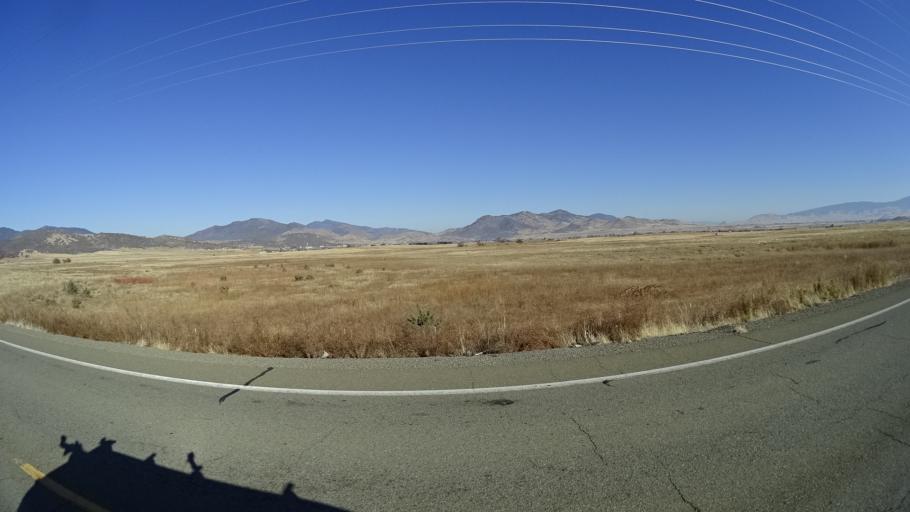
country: US
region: California
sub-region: Siskiyou County
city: Yreka
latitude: 41.7113
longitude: -122.5883
